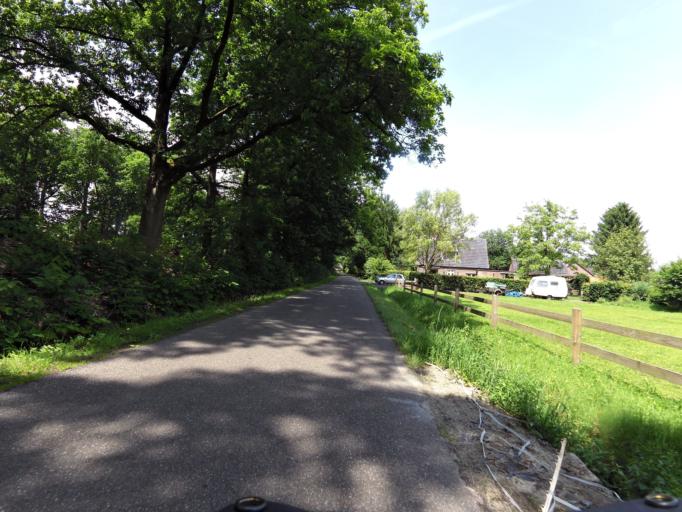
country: NL
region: Gelderland
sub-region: Gemeente Apeldoorn
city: Loenen
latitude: 52.1507
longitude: 6.0363
